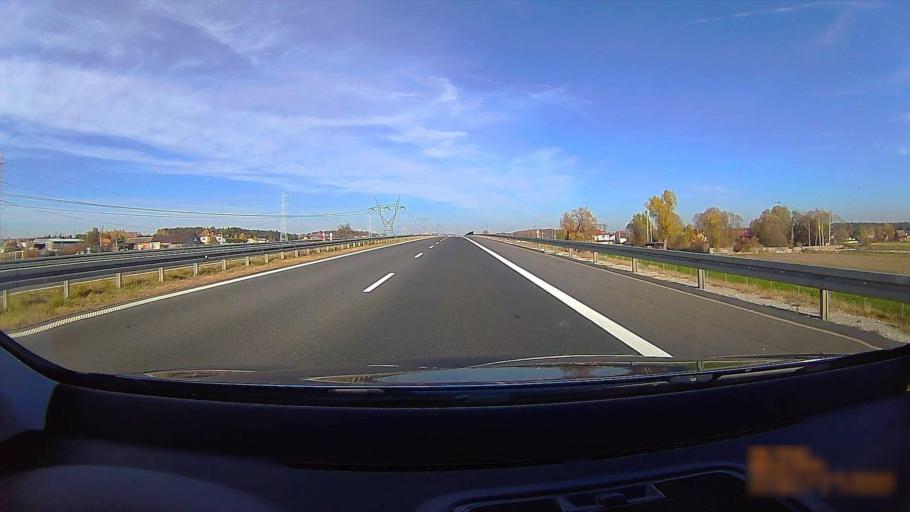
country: PL
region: Greater Poland Voivodeship
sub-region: Powiat ostrowski
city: Przygodzice
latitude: 51.6032
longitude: 17.8534
